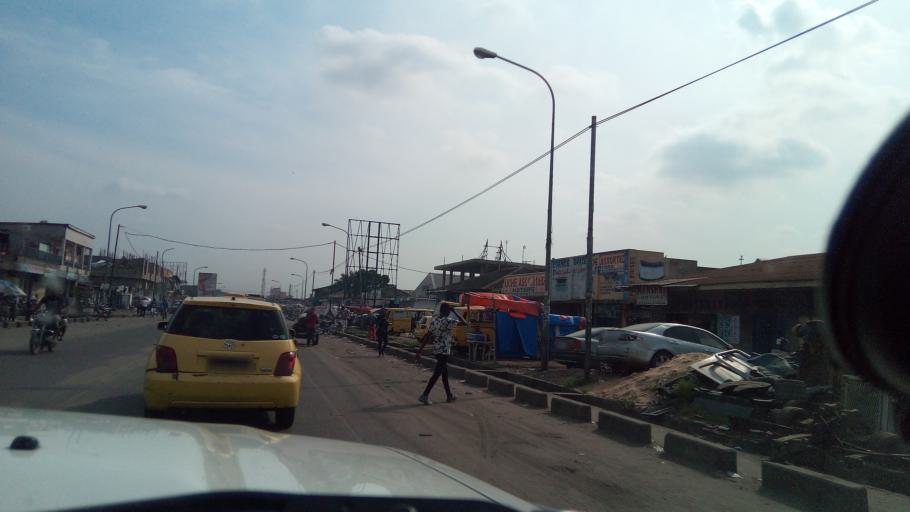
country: CD
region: Kinshasa
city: Kinshasa
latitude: -4.3493
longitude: 15.3111
